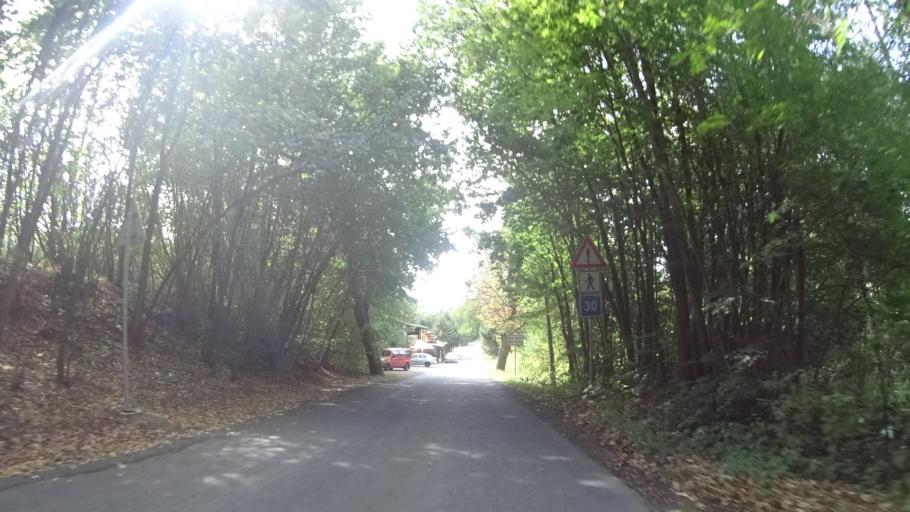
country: CZ
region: Olomoucky
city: Bila Lhota
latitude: 49.7324
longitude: 16.9983
